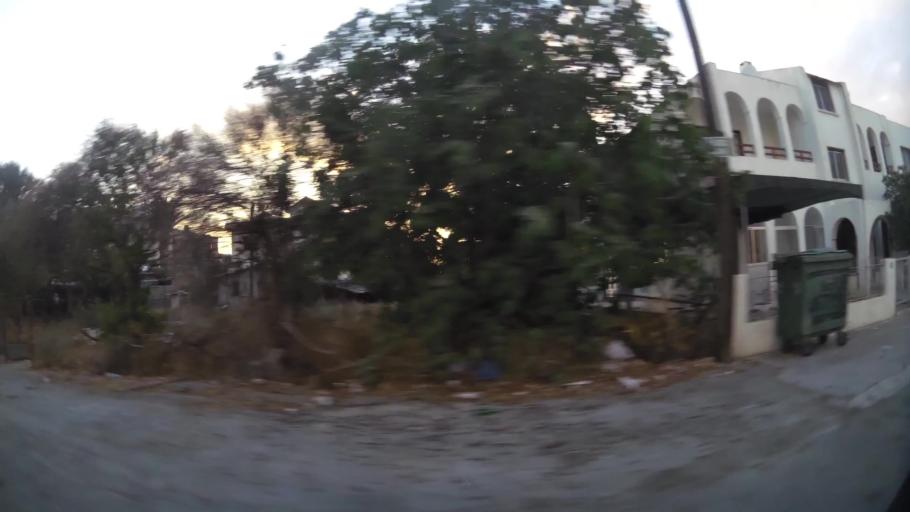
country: CY
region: Lefkosia
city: Nicosia
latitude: 35.1981
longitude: 33.3728
